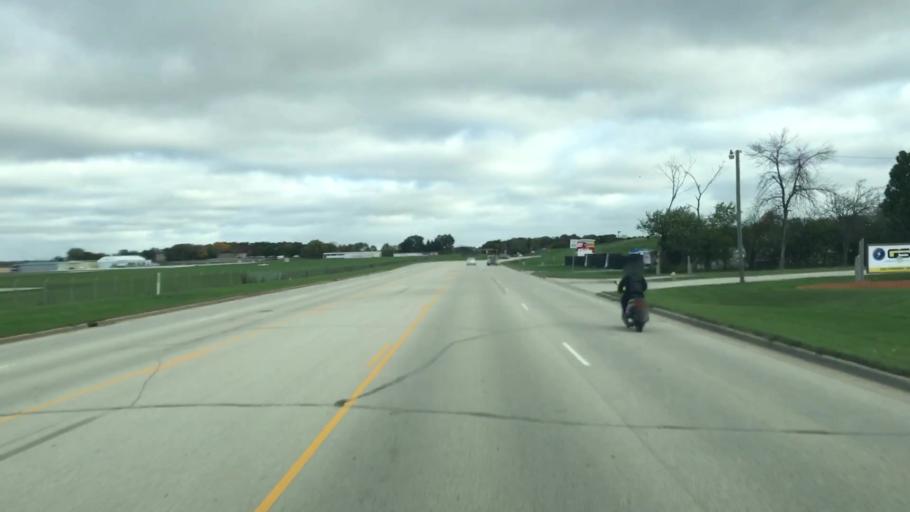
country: US
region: Wisconsin
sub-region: Waukesha County
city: Waukesha
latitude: 43.0360
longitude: -88.2257
